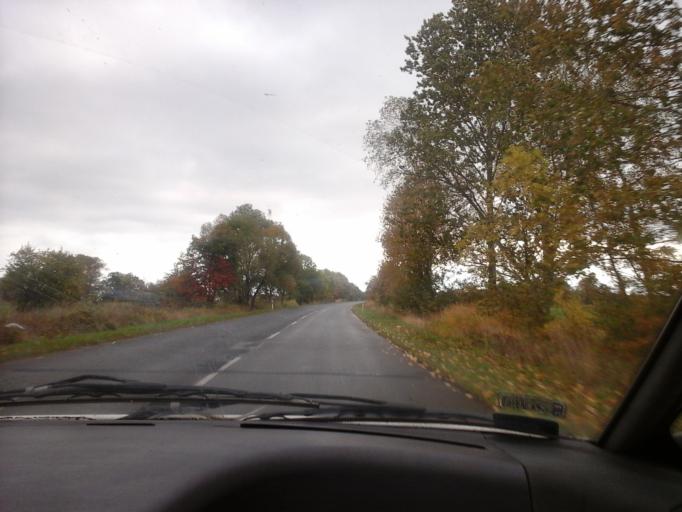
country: PL
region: Pomeranian Voivodeship
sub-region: Powiat gdanski
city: Cedry Wielkie
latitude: 54.3297
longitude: 18.7755
